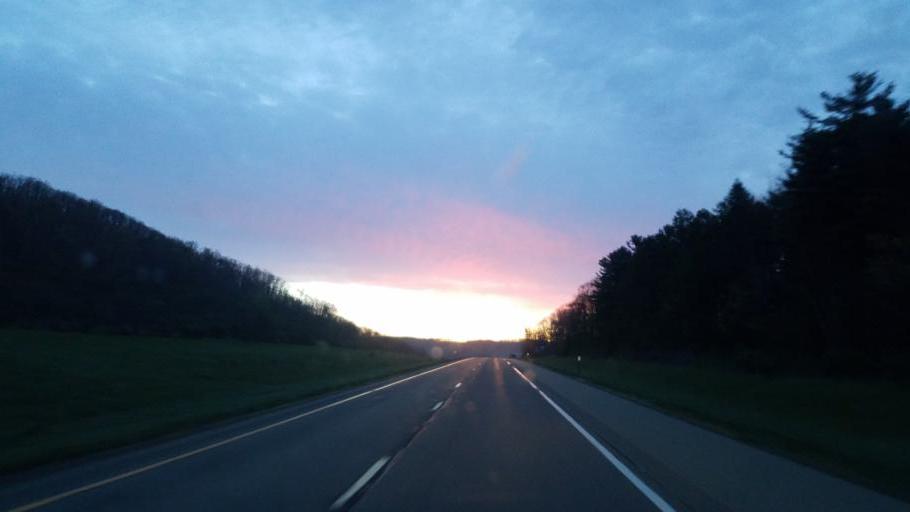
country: US
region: New York
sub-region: Allegany County
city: Cuba
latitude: 42.2194
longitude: -78.2962
